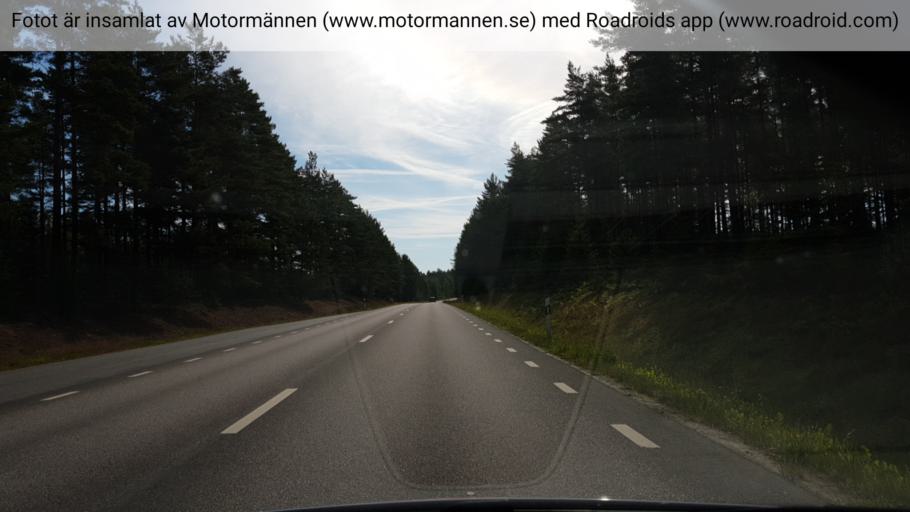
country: SE
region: Vaestra Goetaland
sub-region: Hjo Kommun
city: Hjo
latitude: 58.3415
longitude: 14.2067
